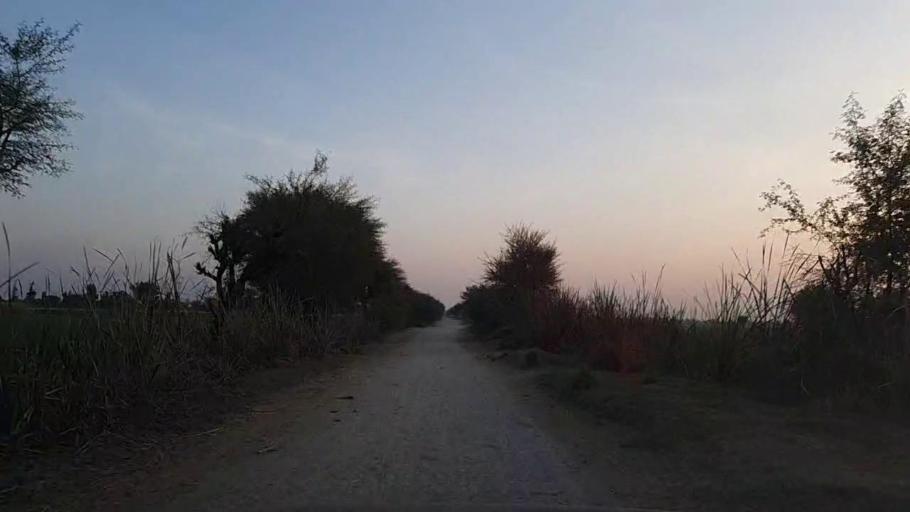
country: PK
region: Sindh
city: Tando Mittha Khan
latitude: 25.9577
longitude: 69.1165
